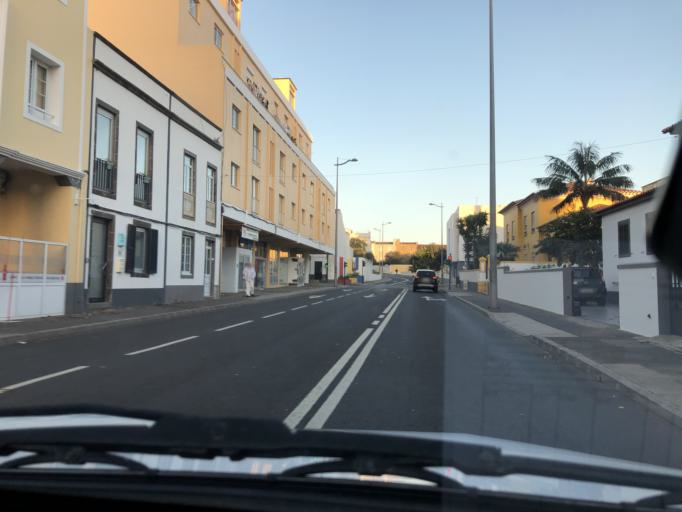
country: PT
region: Azores
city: Ponta Delgada
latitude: 37.7465
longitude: -25.6686
